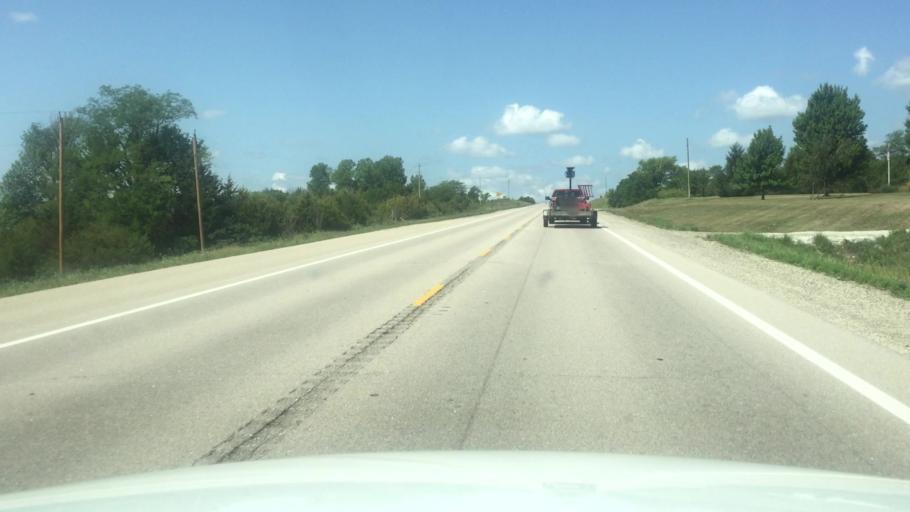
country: US
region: Kansas
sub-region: Nemaha County
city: Sabetha
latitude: 39.8434
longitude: -95.6855
